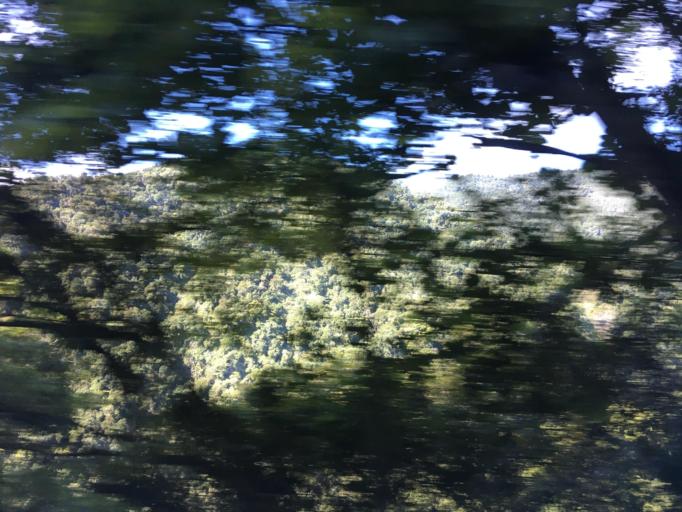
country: TW
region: Taiwan
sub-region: Yilan
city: Yilan
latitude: 24.5560
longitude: 121.5042
